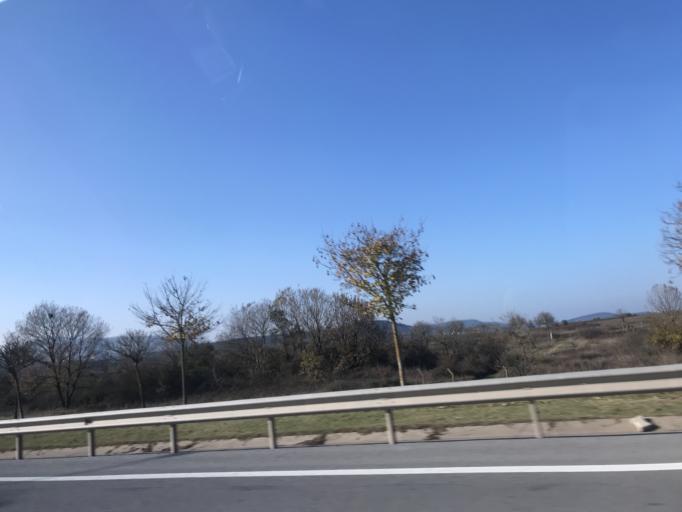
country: TR
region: Kocaeli
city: Balcik
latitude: 40.9391
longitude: 29.3671
